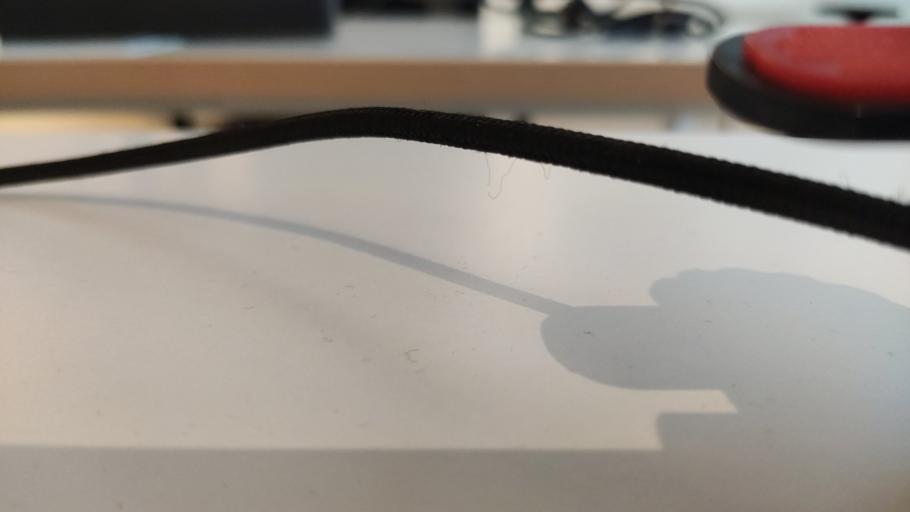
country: RU
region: Moskovskaya
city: Novopetrovskoye
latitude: 55.9321
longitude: 36.4341
